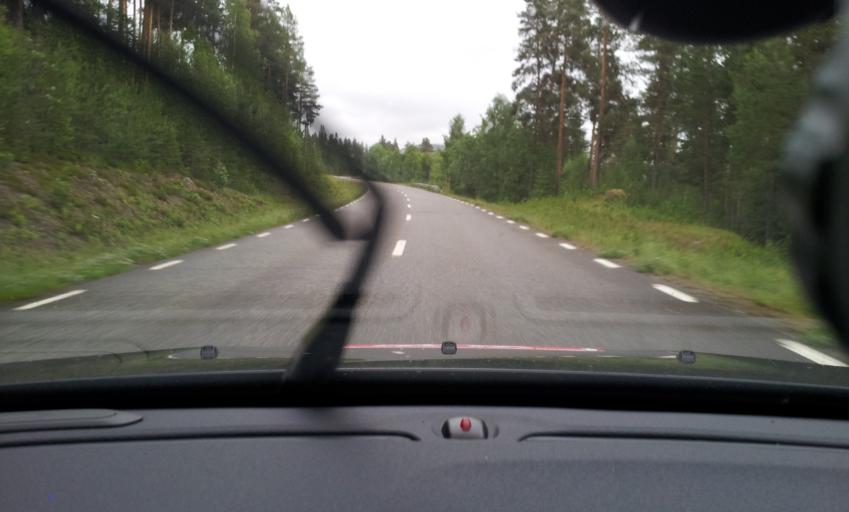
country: SE
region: Jaemtland
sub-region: Stroemsunds Kommun
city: Stroemsund
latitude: 63.3699
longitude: 15.7036
